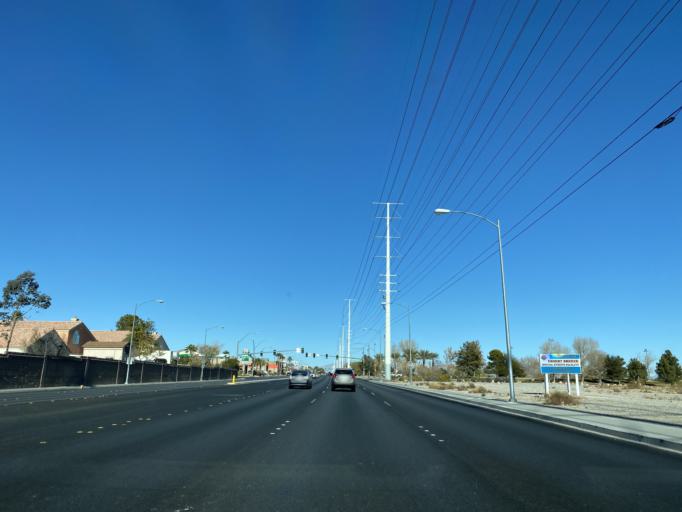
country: US
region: Nevada
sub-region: Clark County
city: Spring Valley
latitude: 36.1207
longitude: -115.2789
